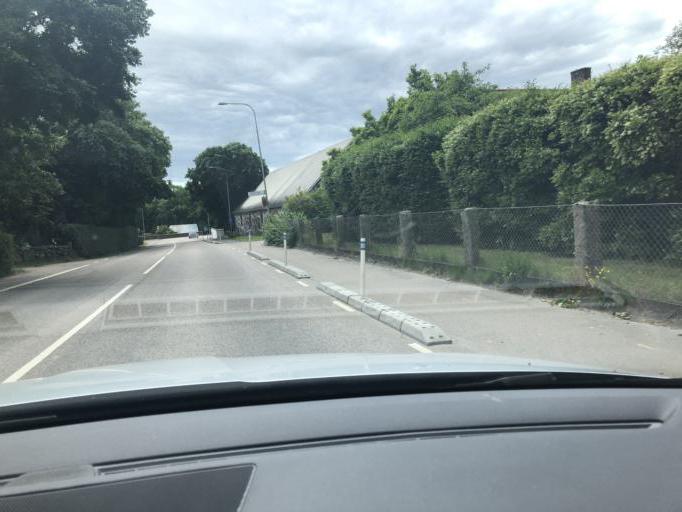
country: SE
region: Blekinge
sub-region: Solvesborgs Kommun
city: Soelvesborg
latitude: 56.0602
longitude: 14.6220
